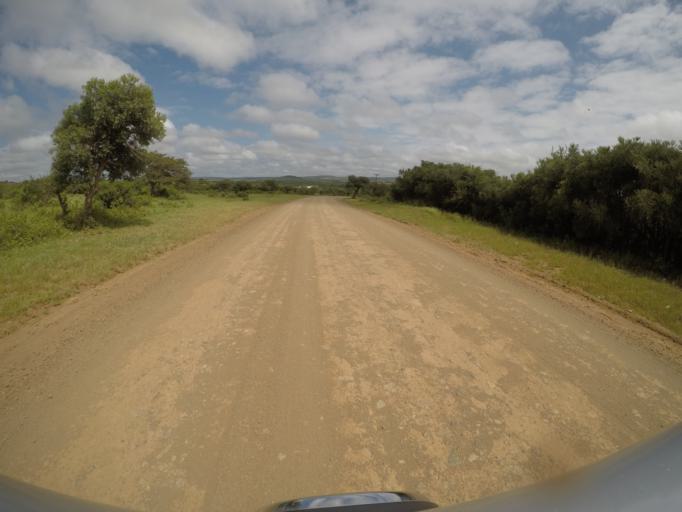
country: ZA
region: KwaZulu-Natal
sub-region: uThungulu District Municipality
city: Empangeni
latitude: -28.6212
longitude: 31.8582
